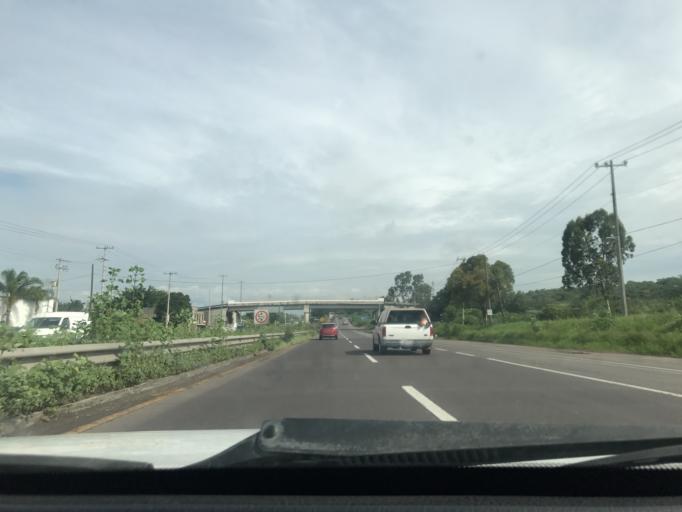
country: MX
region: Morelos
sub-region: Yecapixtla
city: Juan Morales
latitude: 18.8352
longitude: -98.9232
